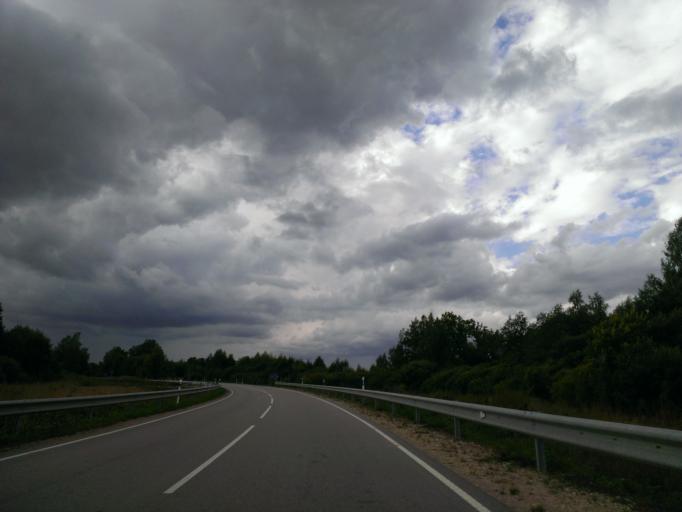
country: LV
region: Malpils
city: Malpils
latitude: 56.8983
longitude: 25.1299
